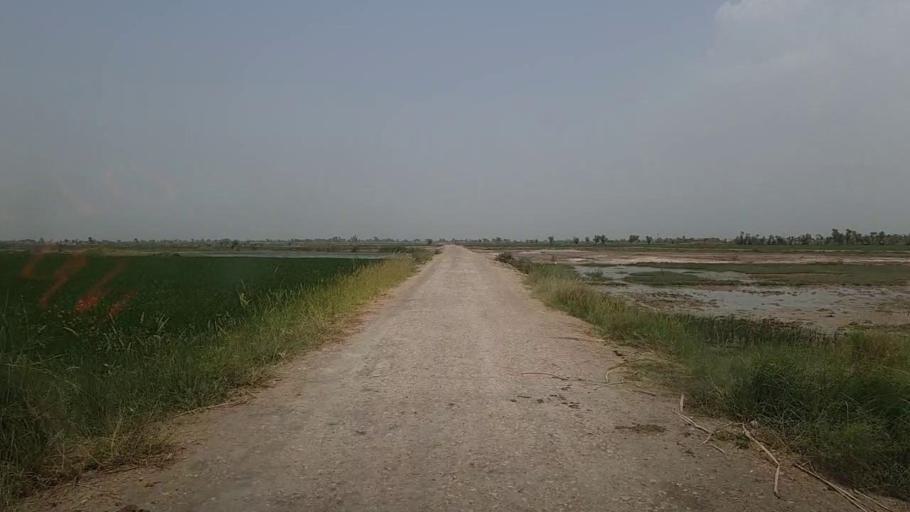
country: PK
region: Sindh
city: Sita Road
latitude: 27.0679
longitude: 67.8628
